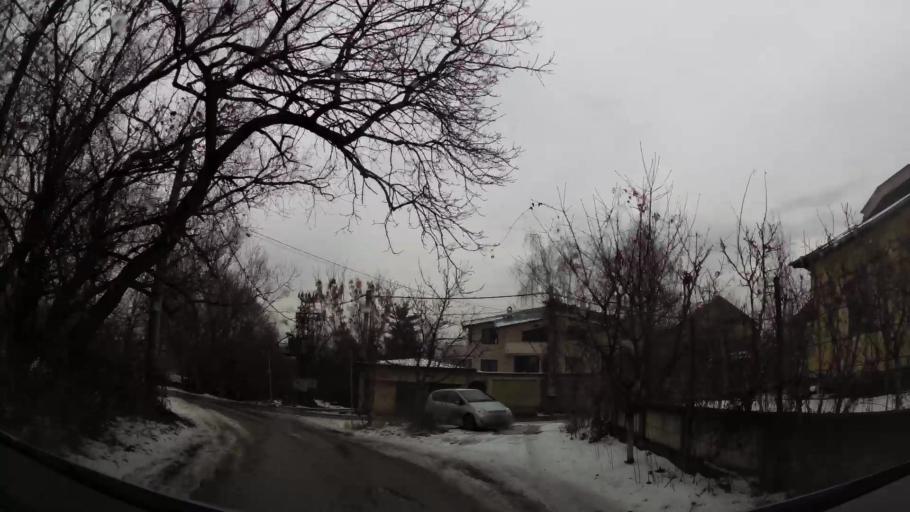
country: BG
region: Sofia-Capital
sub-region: Stolichna Obshtina
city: Sofia
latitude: 42.6517
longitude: 23.2956
